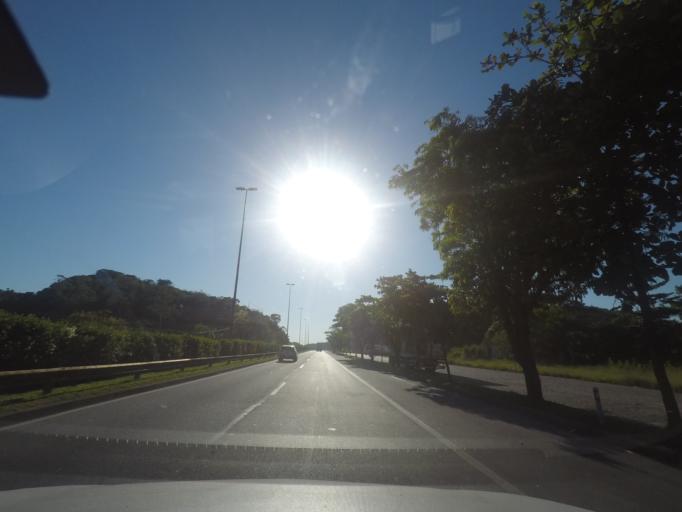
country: BR
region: Rio de Janeiro
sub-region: Petropolis
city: Petropolis
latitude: -22.6528
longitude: -43.1609
